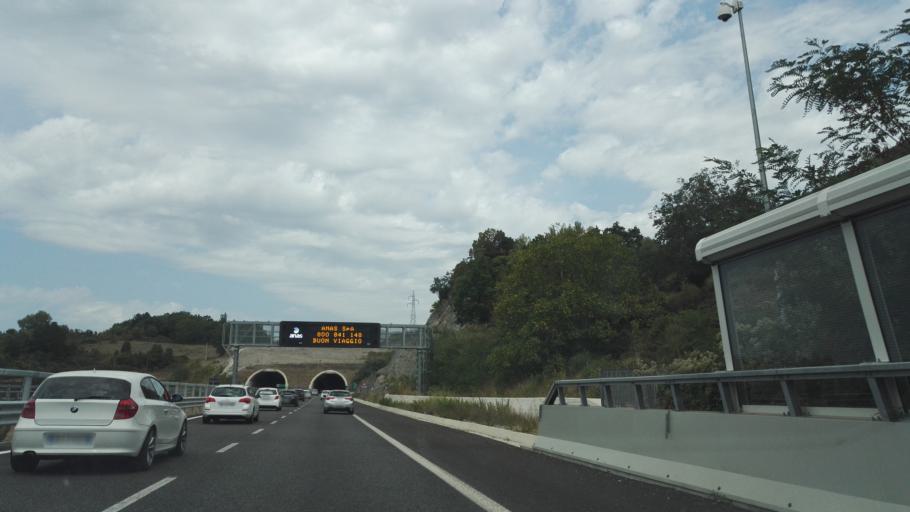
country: IT
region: Basilicate
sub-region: Provincia di Potenza
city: Lauria
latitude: 40.0261
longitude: 15.8774
